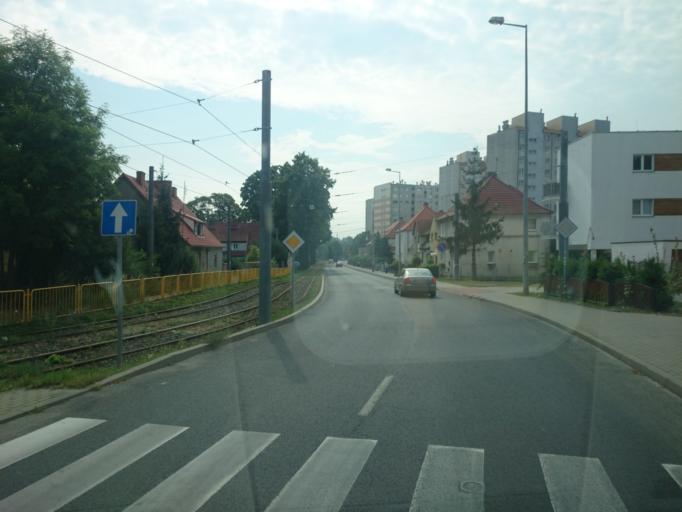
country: PL
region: Lubusz
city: Gorzow Wielkopolski
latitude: 52.7437
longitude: 15.2499
